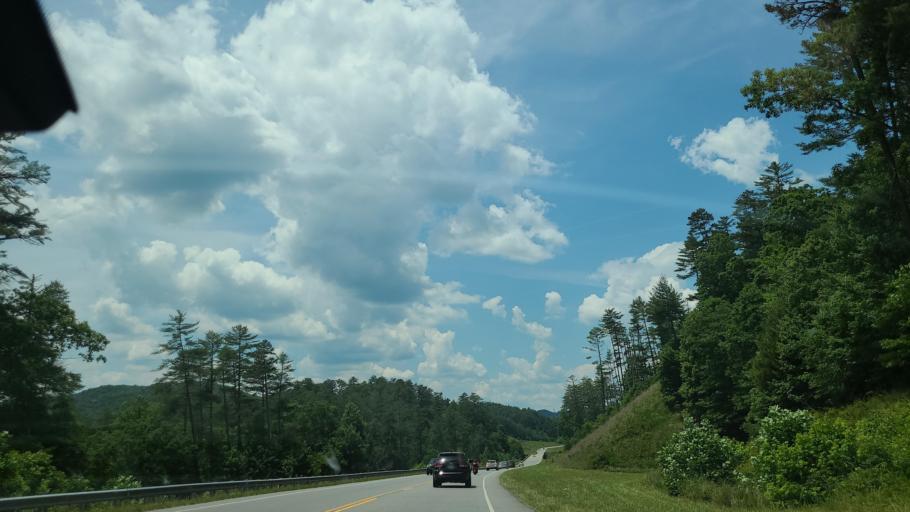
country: US
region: North Carolina
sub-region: Cherokee County
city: Murphy
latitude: 35.0704
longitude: -84.0148
